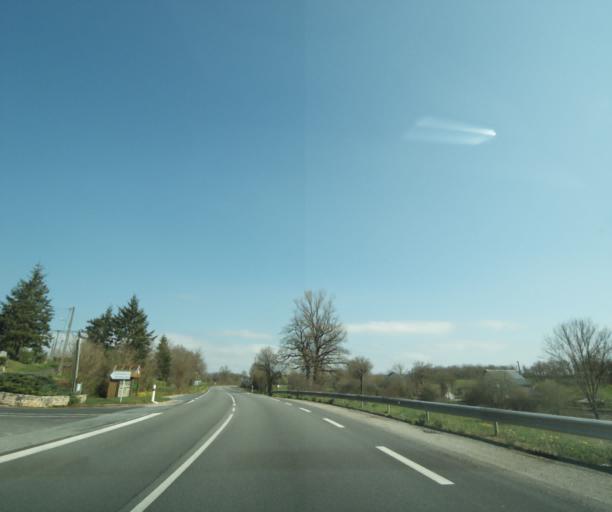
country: FR
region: Midi-Pyrenees
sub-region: Departement de l'Aveyron
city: La Loubiere
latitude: 44.3780
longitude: 2.6540
